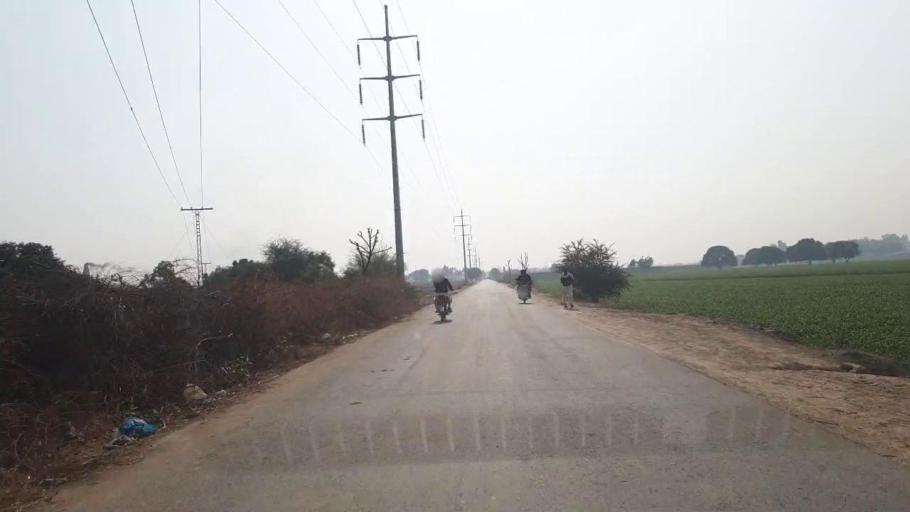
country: PK
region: Sindh
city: Hala
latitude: 25.8319
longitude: 68.4201
